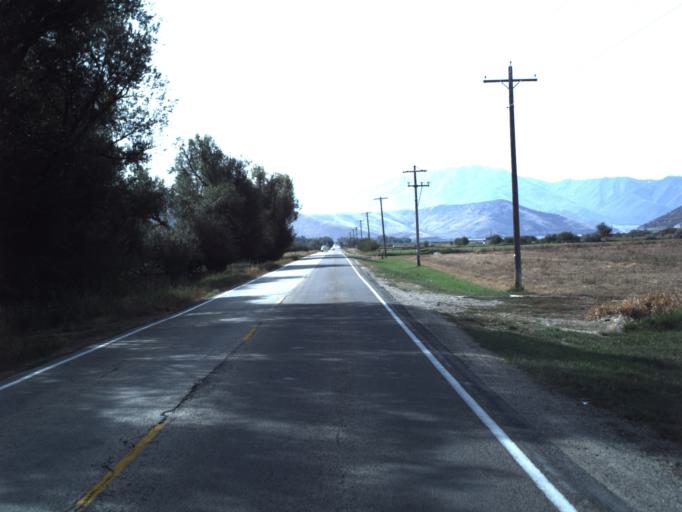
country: US
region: Utah
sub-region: Wasatch County
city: Midway
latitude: 40.4919
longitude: -111.4720
